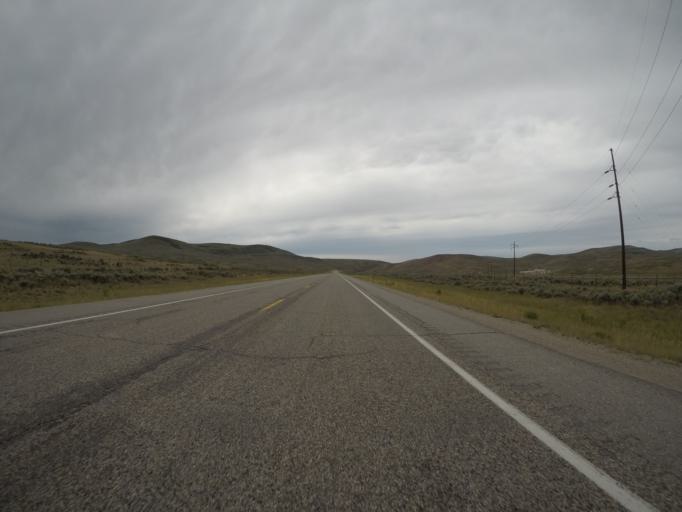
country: US
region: Wyoming
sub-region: Lincoln County
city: Kemmerer
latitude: 41.8171
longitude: -110.7805
